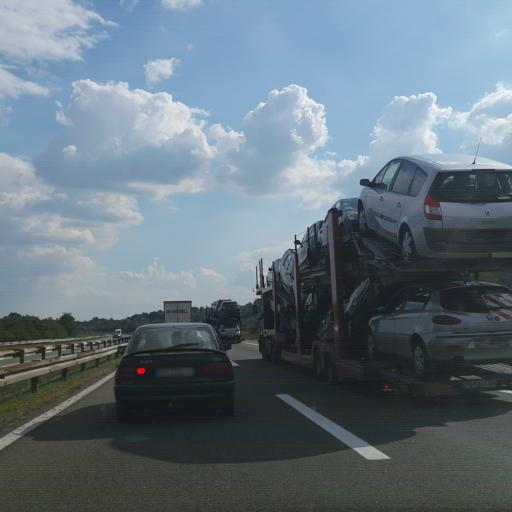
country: RS
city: Lugavcina
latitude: 44.4383
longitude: 21.0501
